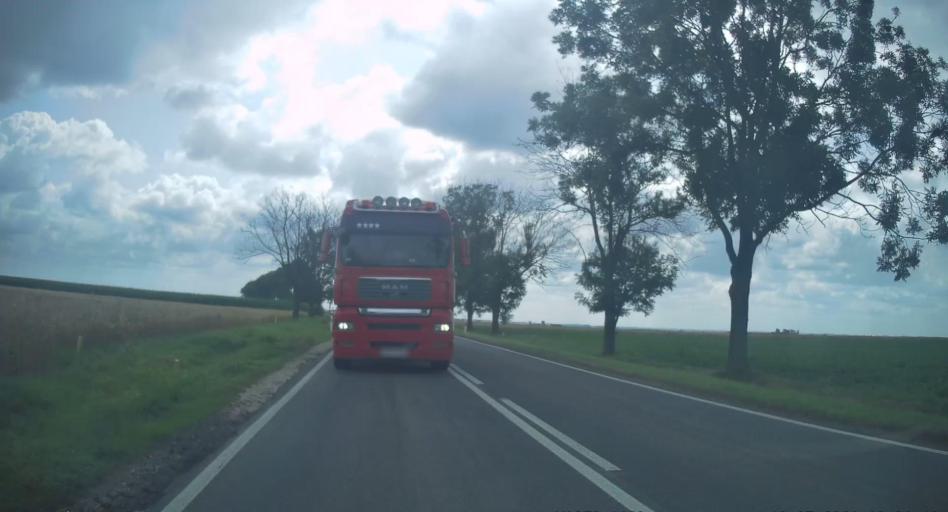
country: PL
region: Opole Voivodeship
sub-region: Powiat prudnicki
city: Glogowek
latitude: 50.3392
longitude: 17.9171
